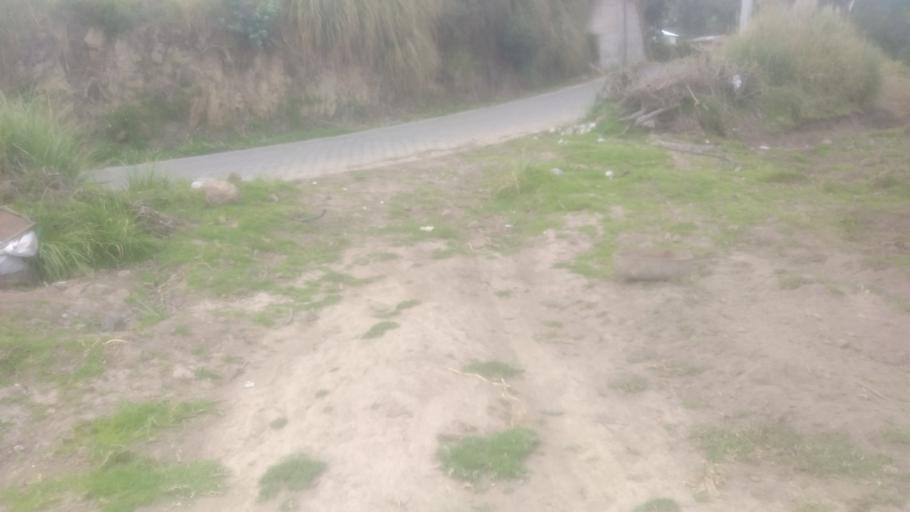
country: EC
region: Chimborazo
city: Riobamba
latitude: -1.7209
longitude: -78.7012
